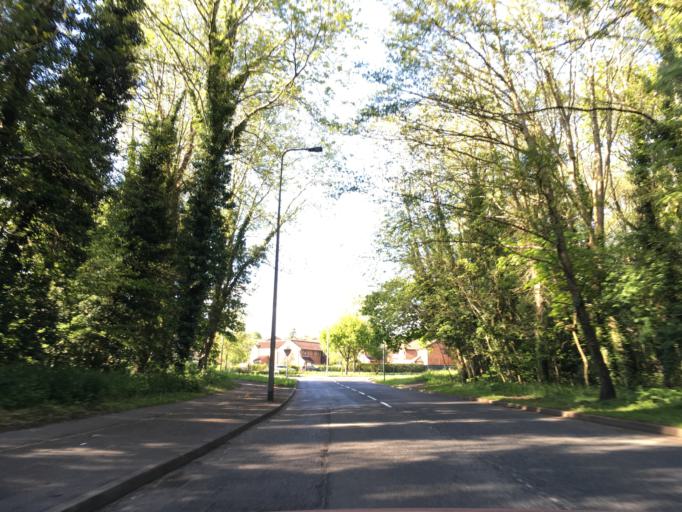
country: GB
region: Wales
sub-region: Cardiff
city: Cardiff
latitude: 51.5295
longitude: -3.1433
